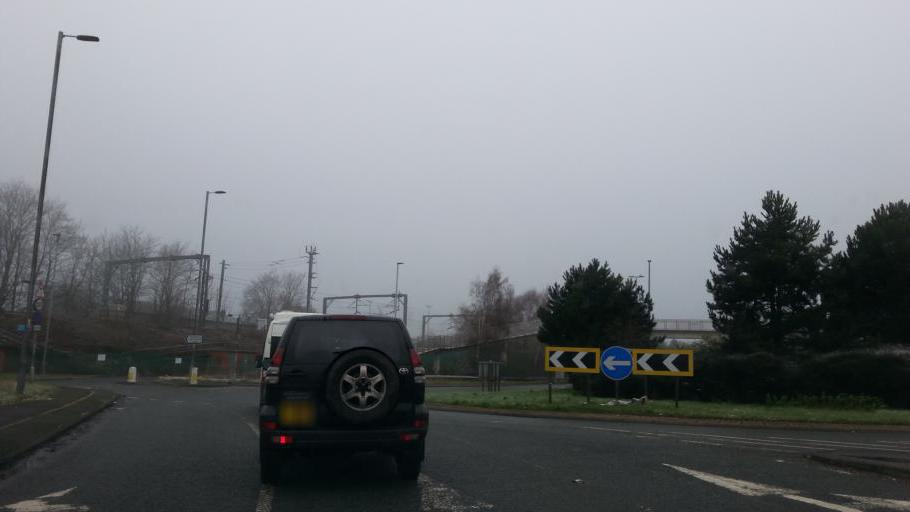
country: GB
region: England
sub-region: Cheshire East
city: Wilmslow
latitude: 53.3205
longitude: -2.2266
